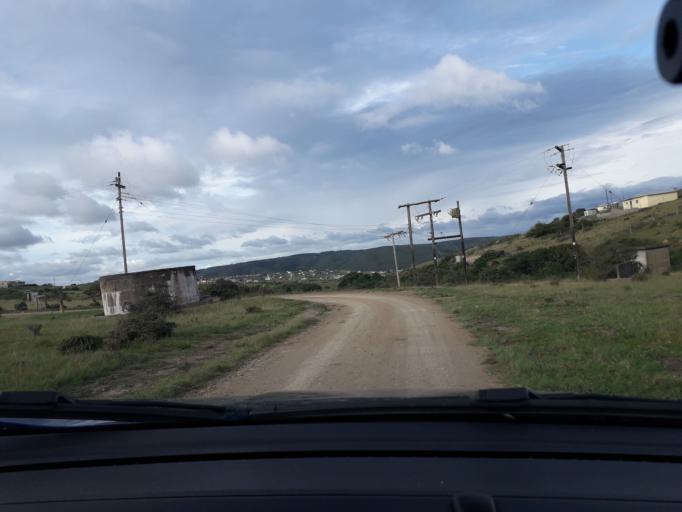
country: ZA
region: Eastern Cape
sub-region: Buffalo City Metropolitan Municipality
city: East London
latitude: -32.8024
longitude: 27.9614
